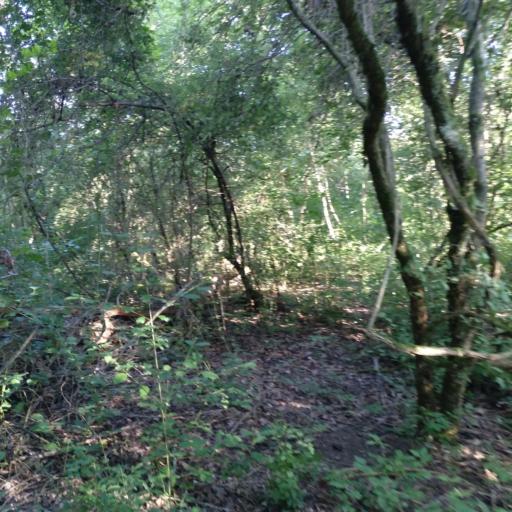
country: FR
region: Rhone-Alpes
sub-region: Departement de l'Ain
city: Miribel
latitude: 45.8012
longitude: 4.9654
